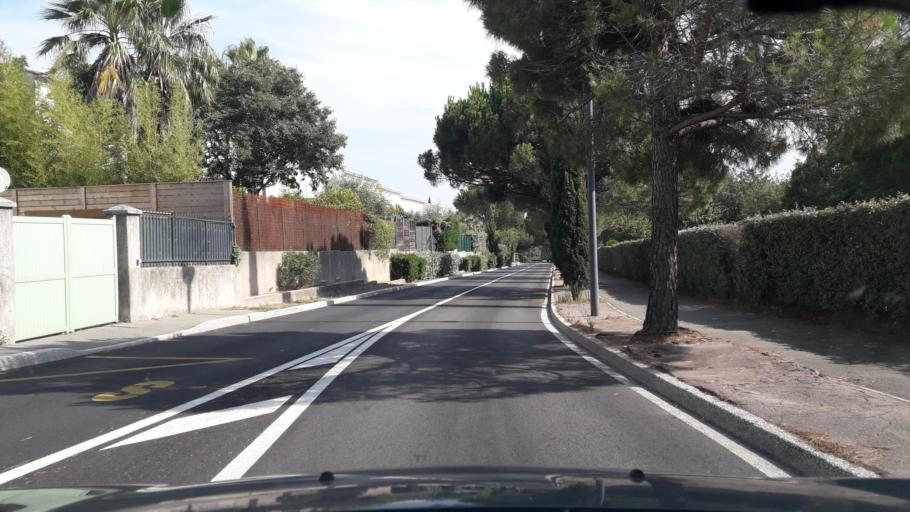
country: FR
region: Provence-Alpes-Cote d'Azur
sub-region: Departement du Var
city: Frejus
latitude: 43.4472
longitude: 6.7490
